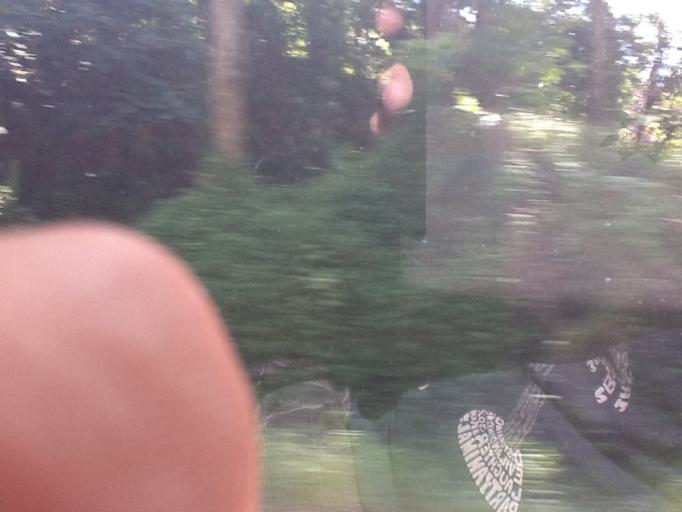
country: TH
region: Phuket
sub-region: Amphoe Kathu
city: Kathu
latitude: 7.9394
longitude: 98.3538
